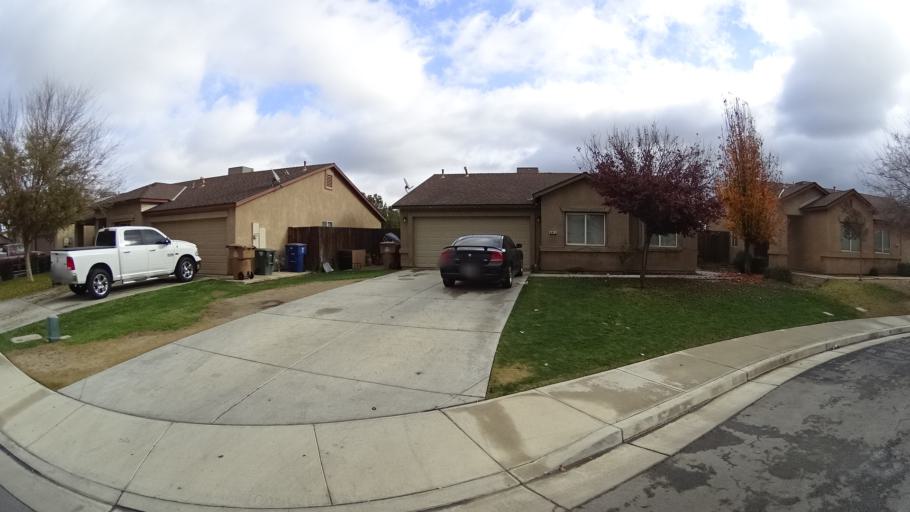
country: US
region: California
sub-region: Kern County
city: Greenfield
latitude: 35.2925
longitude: -118.9979
